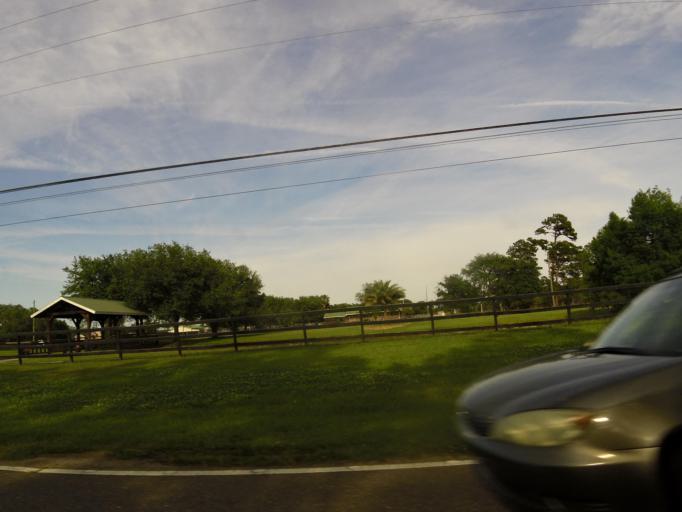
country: US
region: Florida
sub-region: Duval County
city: Atlantic Beach
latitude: 30.4665
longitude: -81.4697
